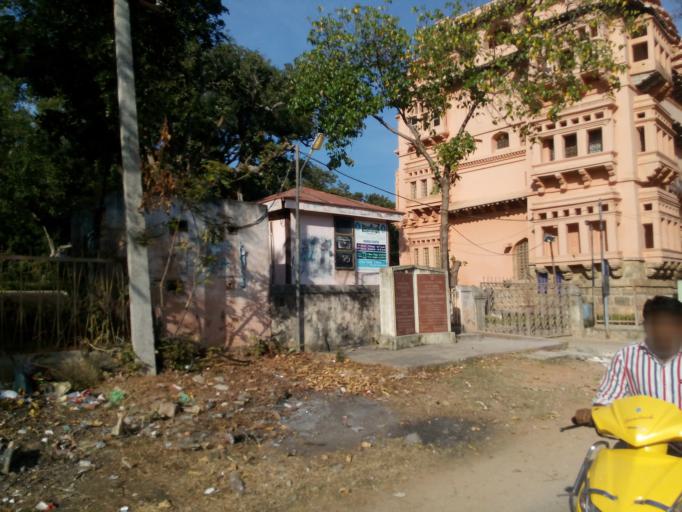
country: IN
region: Andhra Pradesh
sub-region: Chittoor
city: Narasingapuram
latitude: 13.5823
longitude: 79.3043
